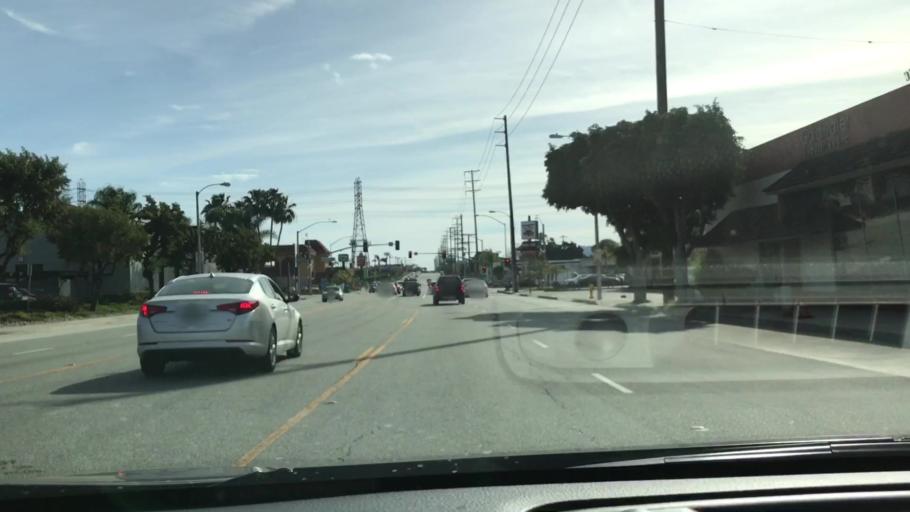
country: US
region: California
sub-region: Los Angeles County
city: Gardena
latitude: 33.8741
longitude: -118.3092
